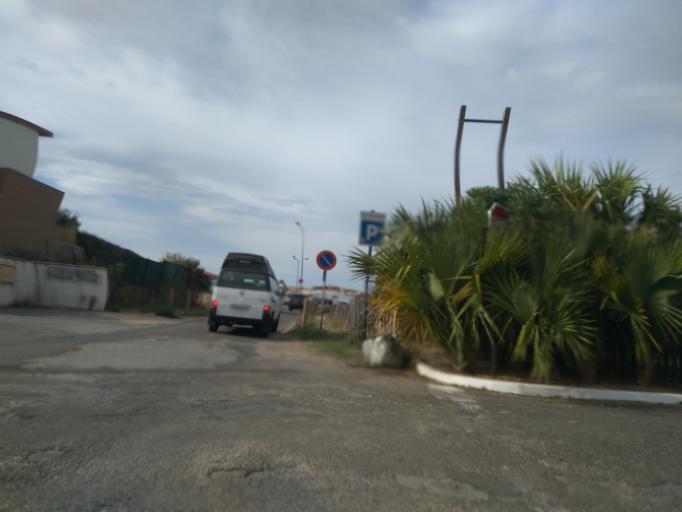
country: FR
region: Aquitaine
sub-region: Departement des Landes
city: Capbreton
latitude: 43.6355
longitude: -1.4460
